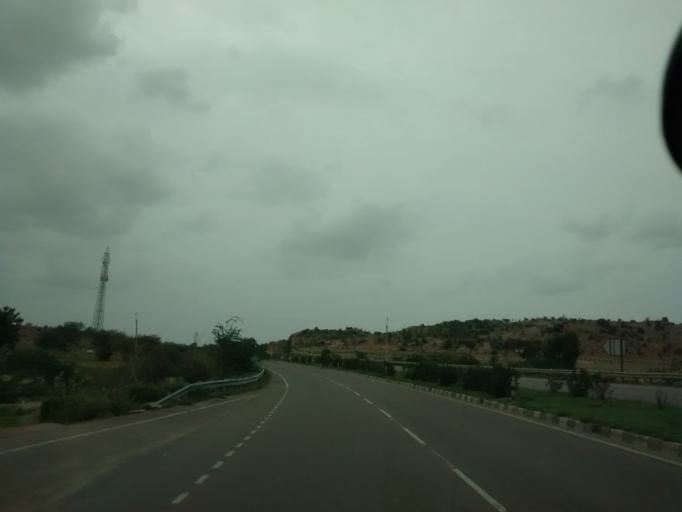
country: IN
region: Andhra Pradesh
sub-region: Kurnool
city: Ramapuram
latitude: 15.1812
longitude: 77.6883
